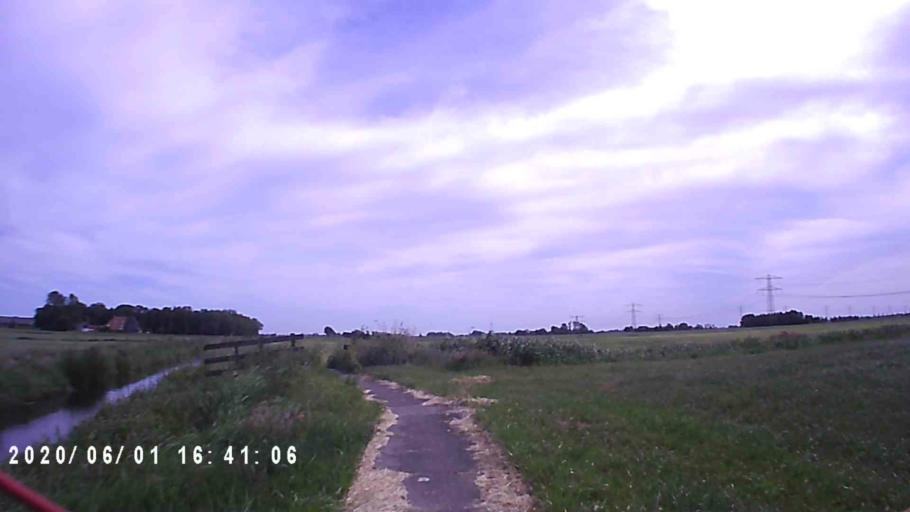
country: NL
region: Friesland
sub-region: Gemeente Boarnsterhim
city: Warten
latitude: 53.1853
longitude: 5.8777
